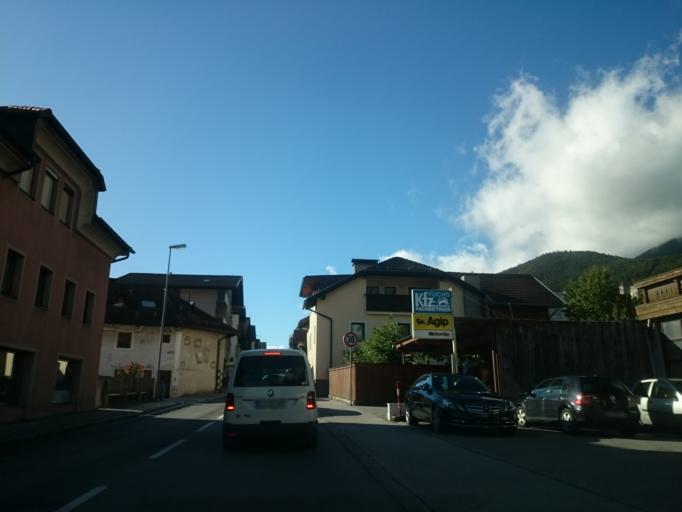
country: AT
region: Tyrol
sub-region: Politischer Bezirk Innsbruck Land
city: Unterperfuss
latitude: 47.2726
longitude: 11.2455
